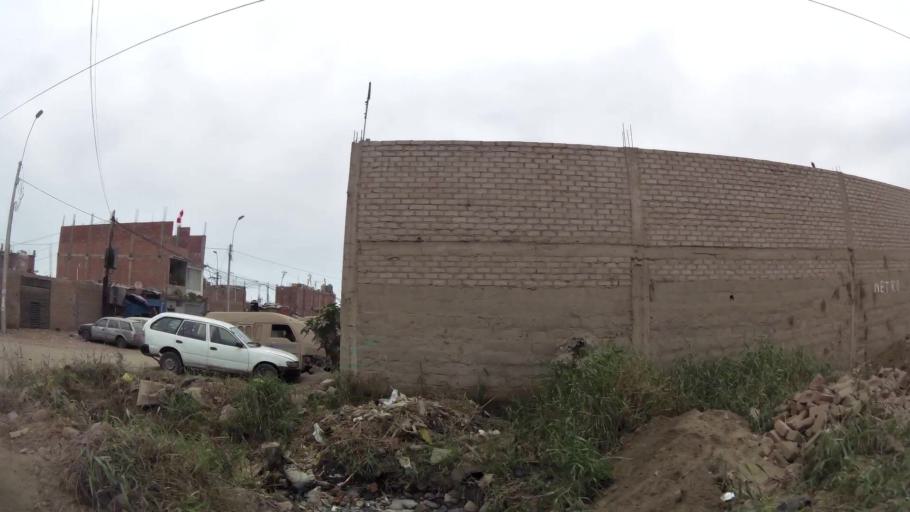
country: PE
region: Lima
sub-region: Lima
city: Surco
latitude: -12.2031
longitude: -76.9671
